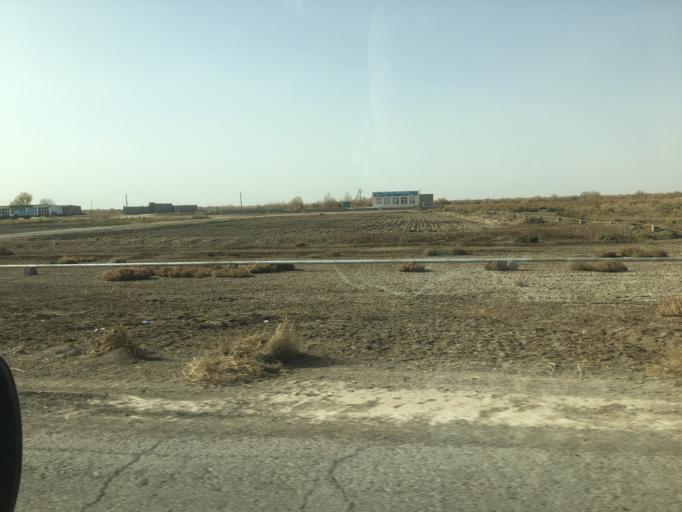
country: TM
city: Akdepe
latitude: 41.6495
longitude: 58.6665
